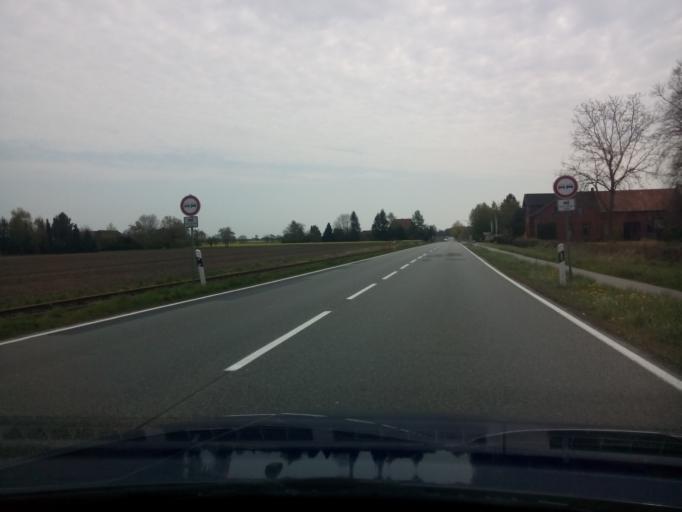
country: DE
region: Lower Saxony
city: Syke
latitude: 52.8987
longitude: 8.8454
